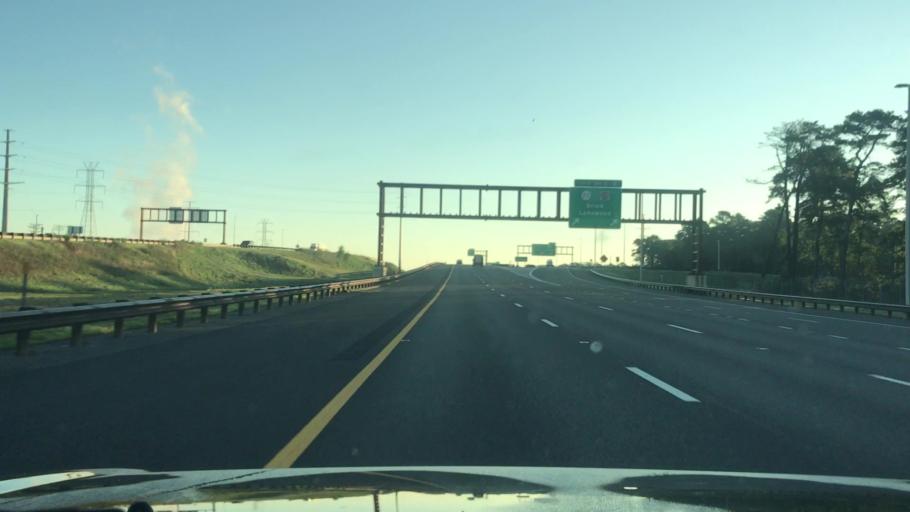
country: US
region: New Jersey
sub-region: Ocean County
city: Leisure Village
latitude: 40.0516
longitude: -74.1703
